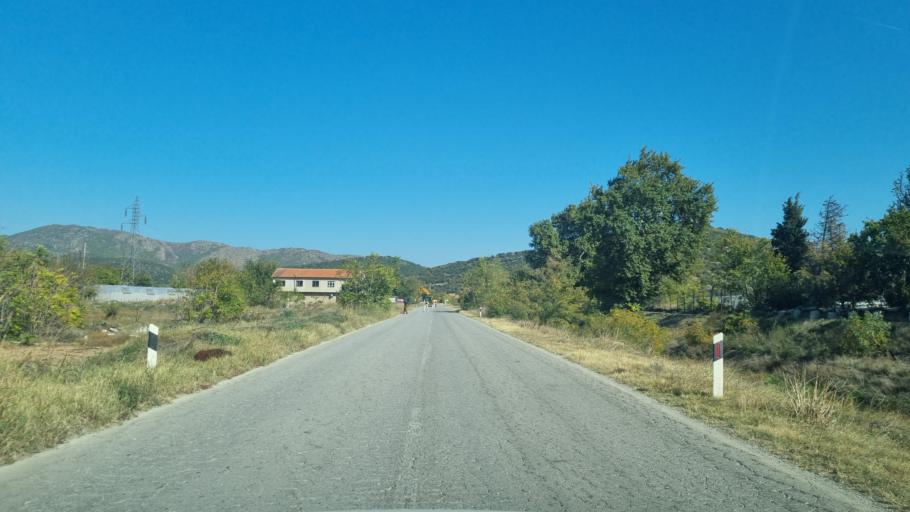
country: MK
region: Bogdanci
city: Bogdanci
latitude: 41.1976
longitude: 22.5850
